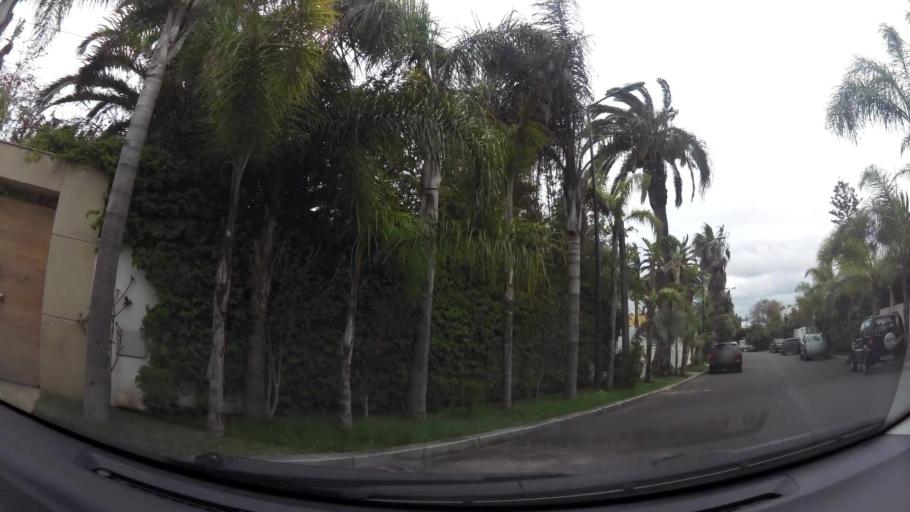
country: MA
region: Grand Casablanca
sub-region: Casablanca
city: Casablanca
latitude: 33.5838
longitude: -7.6612
